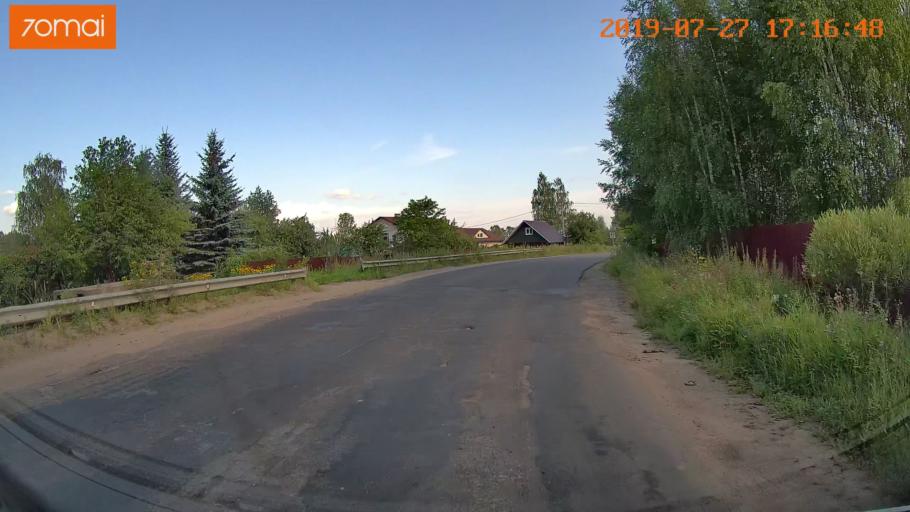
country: RU
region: Ivanovo
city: Novo-Talitsy
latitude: 57.0428
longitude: 40.8899
